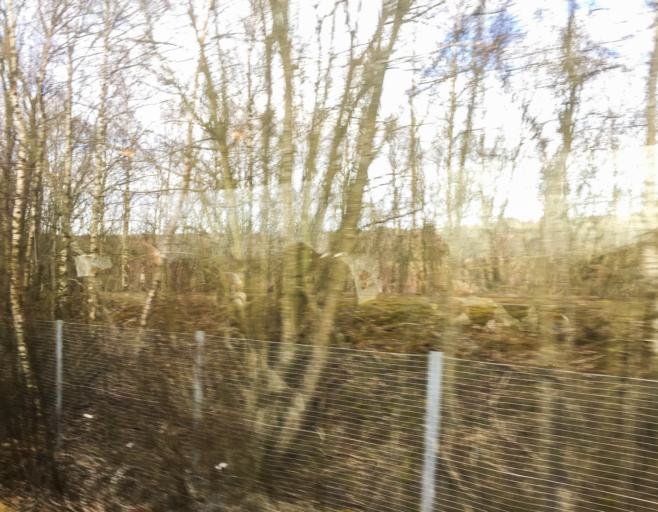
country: GB
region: Scotland
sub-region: North Lanarkshire
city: Newarthill
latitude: 55.7845
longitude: -3.9472
